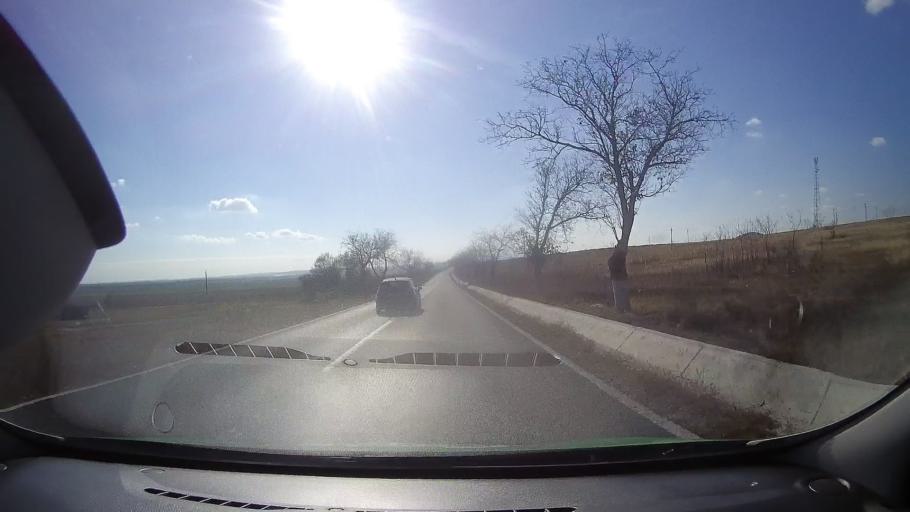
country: RO
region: Tulcea
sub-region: Comuna Ceamurlia de Jos
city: Ceamurlia de Jos
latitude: 44.8108
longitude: 28.6914
